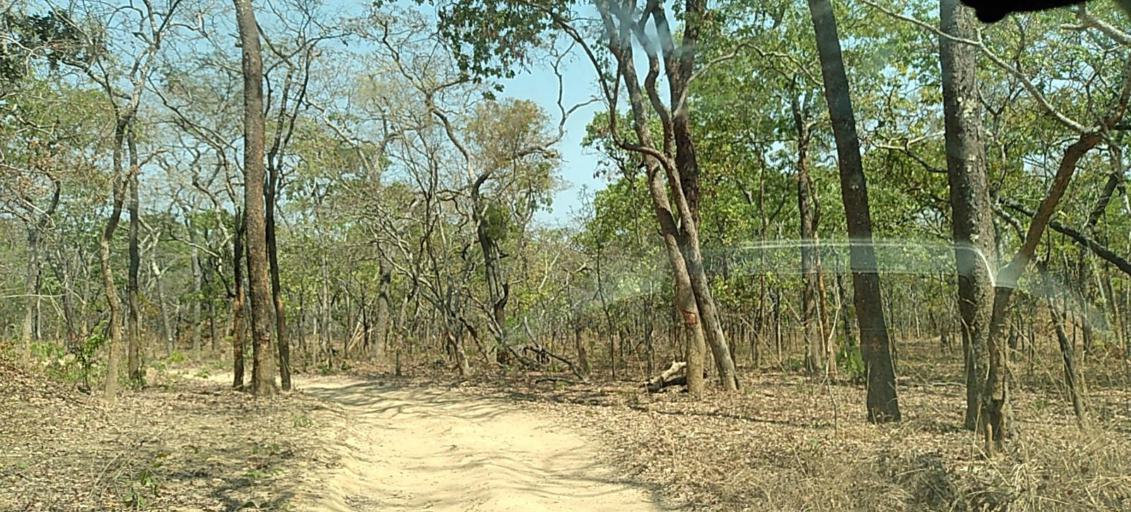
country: ZM
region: North-Western
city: Kasempa
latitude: -13.3915
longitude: 25.6268
